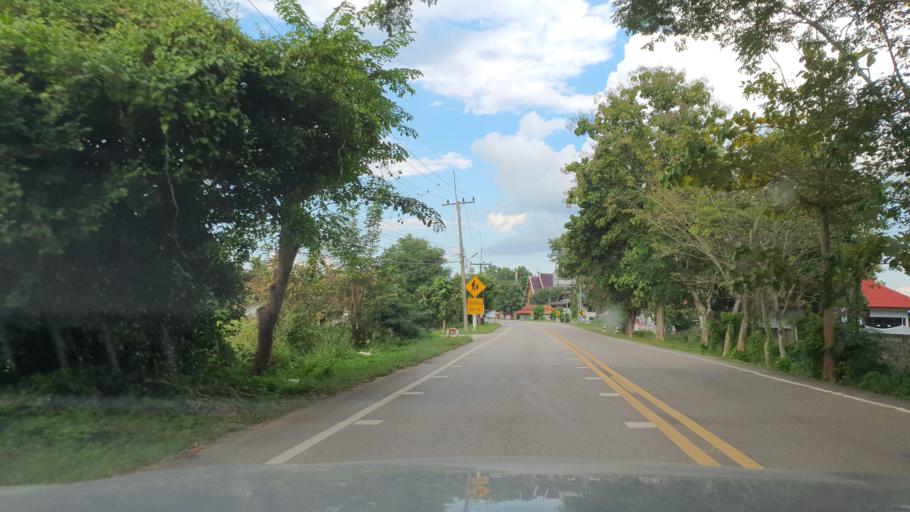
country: TH
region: Phayao
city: Phayao
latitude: 19.1774
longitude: 99.8354
